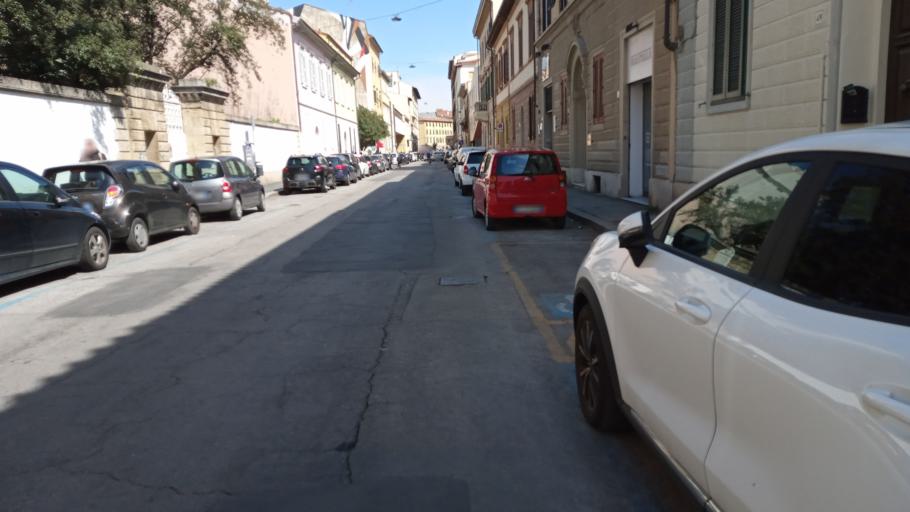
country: IT
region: Tuscany
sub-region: Provincia di Livorno
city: Livorno
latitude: 43.5418
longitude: 10.3131
